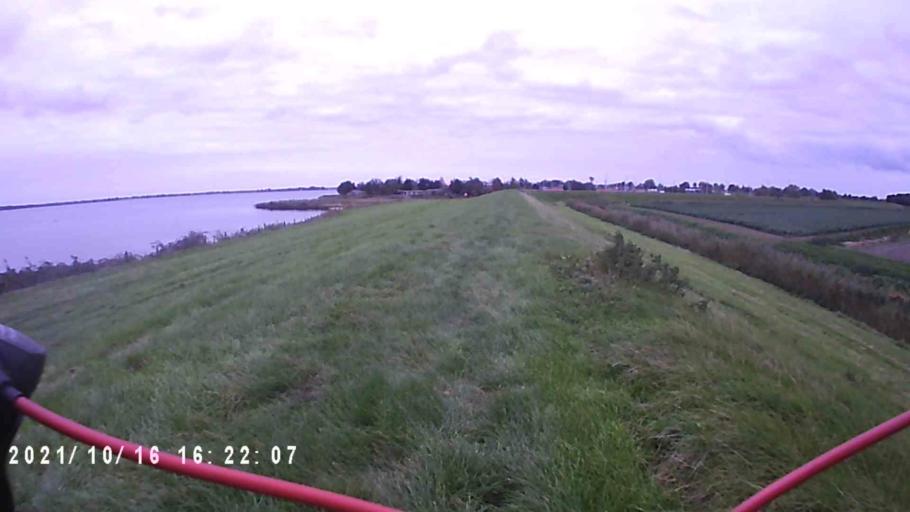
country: NL
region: Friesland
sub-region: Gemeente Dongeradeel
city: Anjum
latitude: 53.3872
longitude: 6.1560
